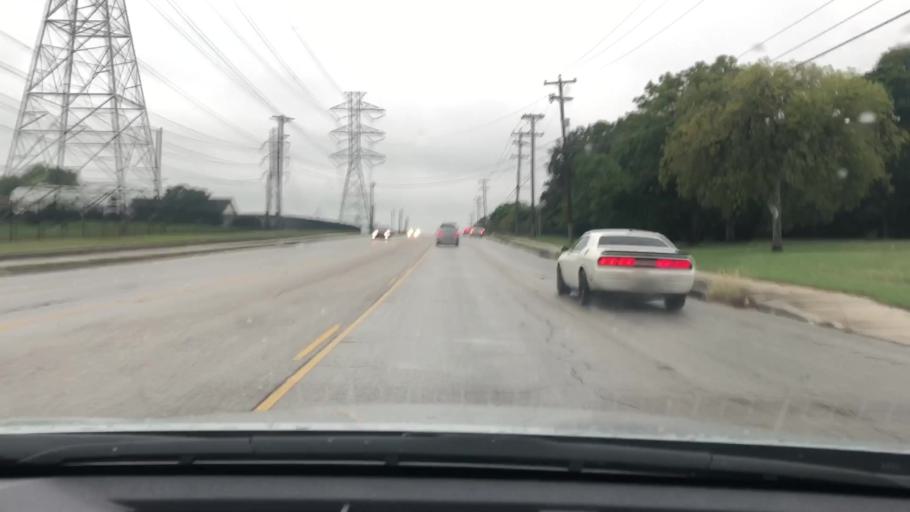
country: US
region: Texas
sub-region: Bexar County
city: Windcrest
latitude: 29.5398
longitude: -98.3638
